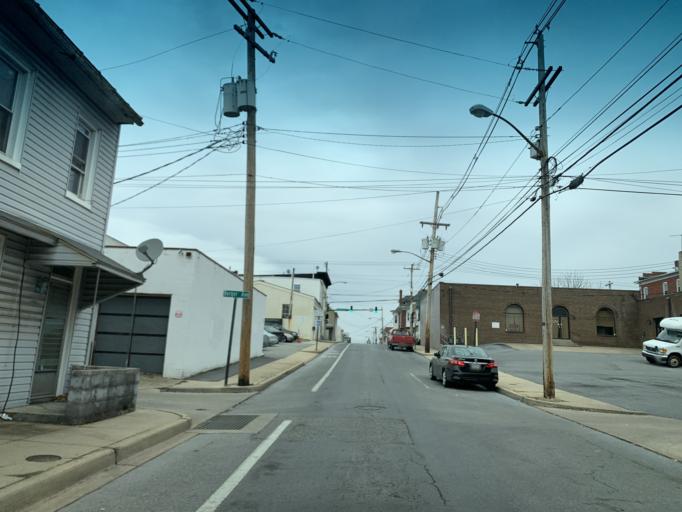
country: US
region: Maryland
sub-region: Washington County
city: Hagerstown
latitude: 39.6374
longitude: -77.7206
